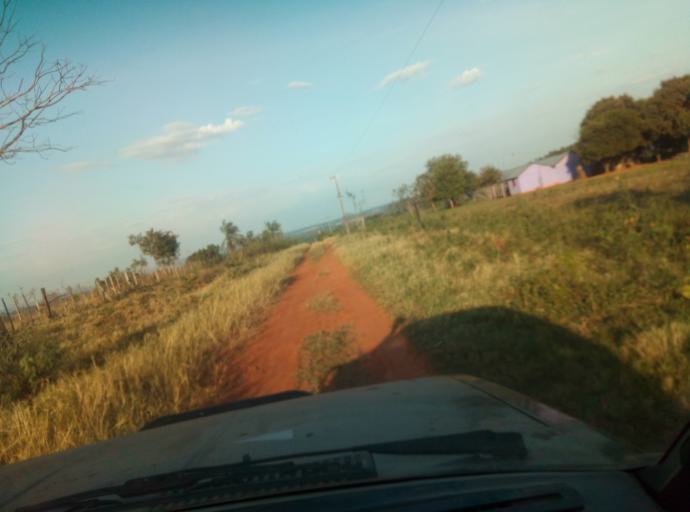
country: PY
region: Caaguazu
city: Doctor Cecilio Baez
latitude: -25.1525
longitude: -56.2437
